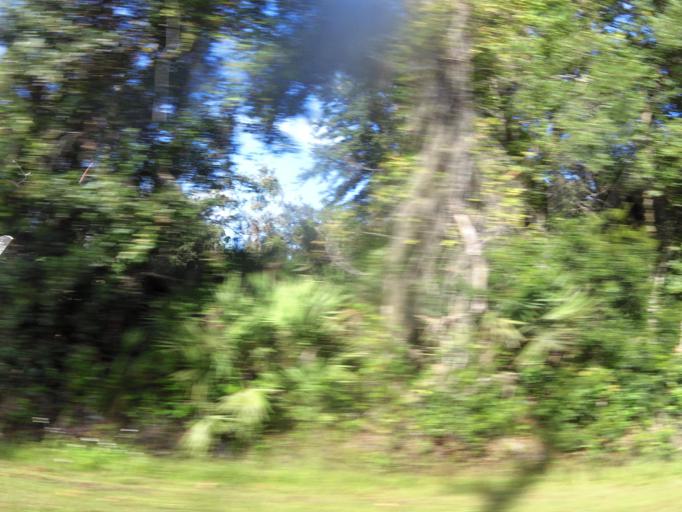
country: US
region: Florida
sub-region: Clay County
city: Green Cove Springs
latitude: 29.9166
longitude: -81.5413
